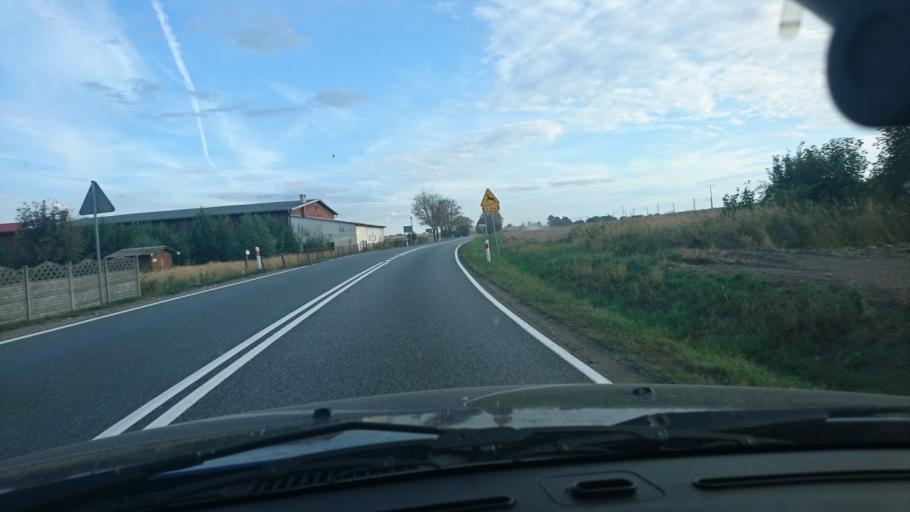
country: PL
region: Opole Voivodeship
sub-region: Powiat kluczborski
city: Byczyna
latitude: 51.1353
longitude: 18.1993
